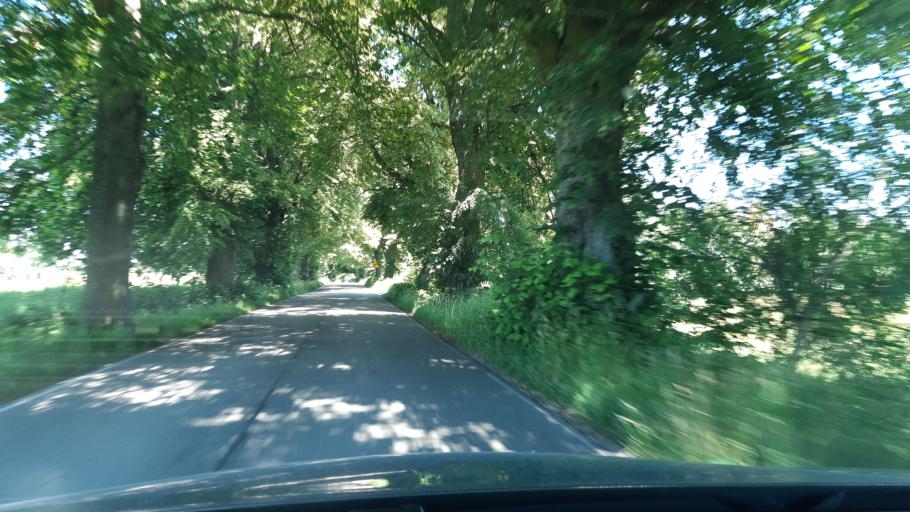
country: PL
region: Warmian-Masurian Voivodeship
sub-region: Powiat gizycki
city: Ryn
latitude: 53.9115
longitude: 21.6766
